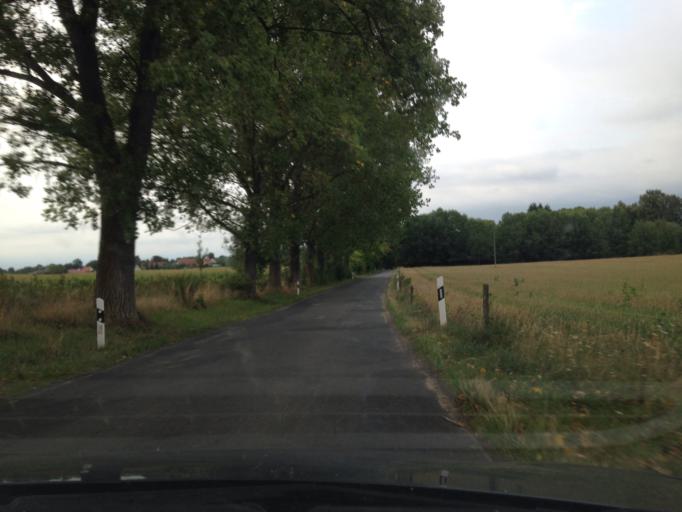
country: DE
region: Mecklenburg-Vorpommern
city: Loitz
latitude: 53.3129
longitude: 13.4189
